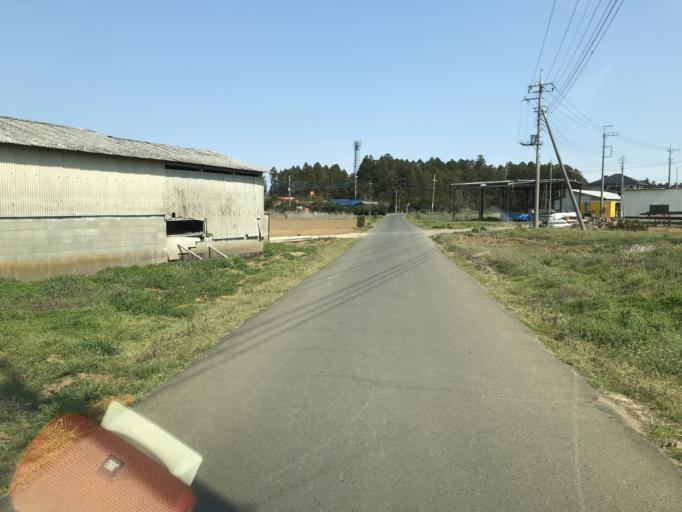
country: JP
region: Chiba
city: Sawara
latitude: 35.8411
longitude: 140.5246
